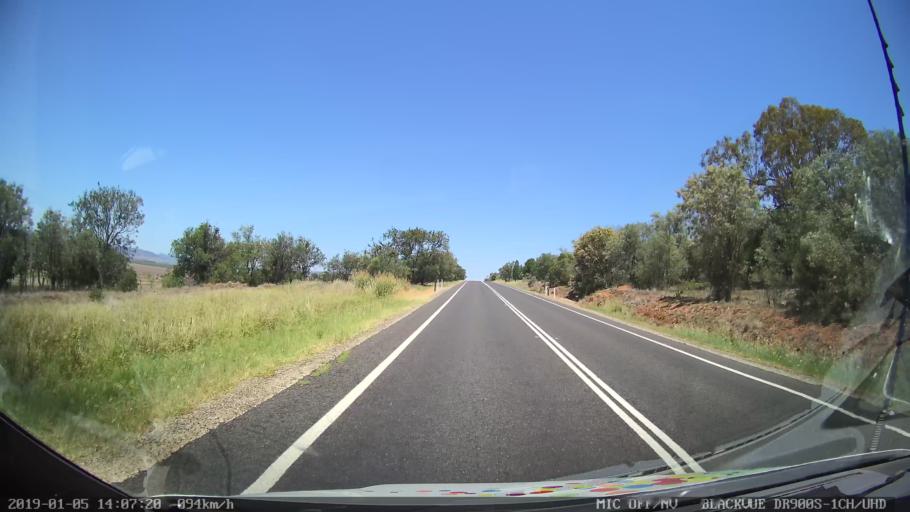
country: AU
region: New South Wales
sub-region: Gunnedah
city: Gunnedah
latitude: -31.2216
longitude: 150.4052
